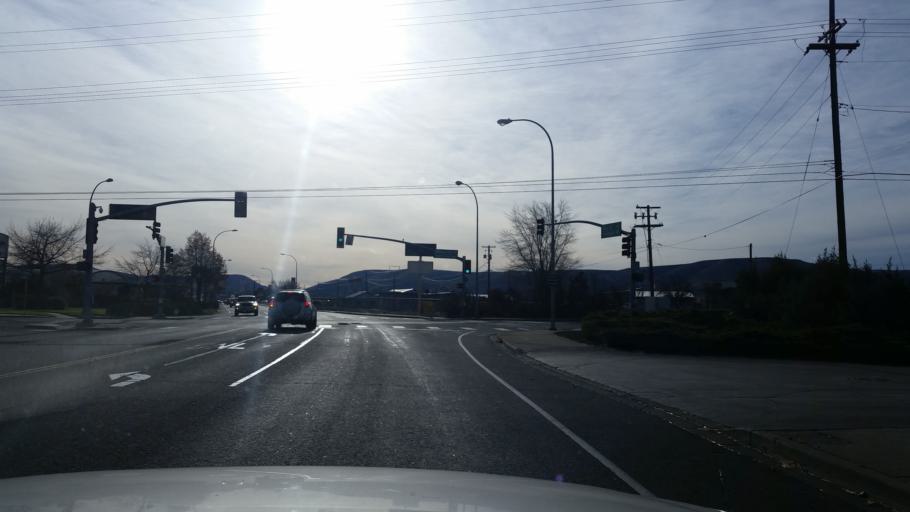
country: US
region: Washington
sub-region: Kittitas County
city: Ellensburg
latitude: 46.9848
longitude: -120.5481
